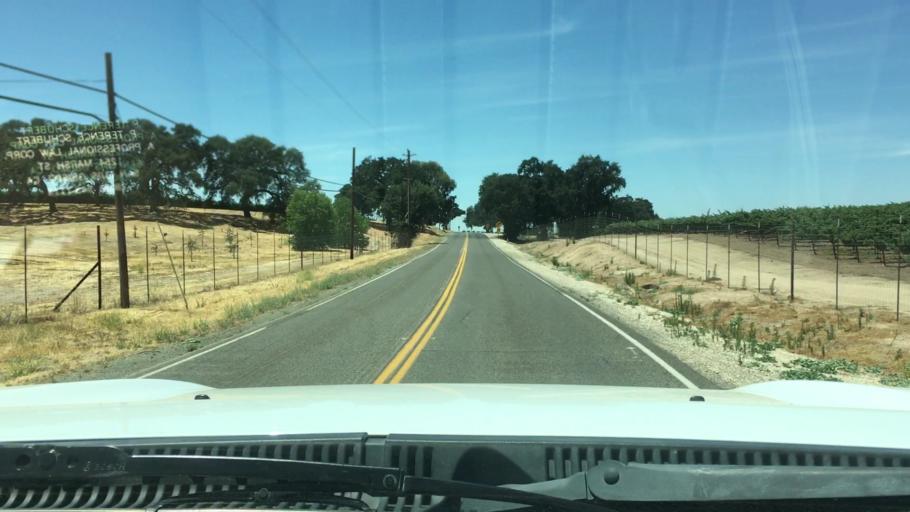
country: US
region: California
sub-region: San Luis Obispo County
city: Paso Robles
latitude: 35.5753
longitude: -120.6122
